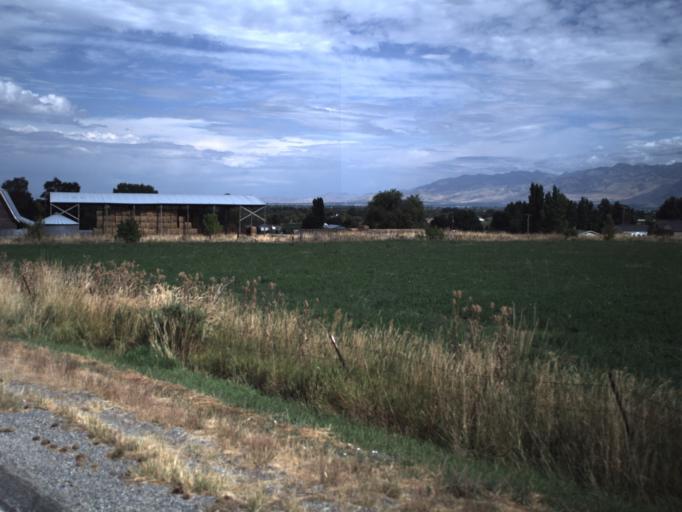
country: US
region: Utah
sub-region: Cache County
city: Wellsville
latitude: 41.6182
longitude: -111.9344
